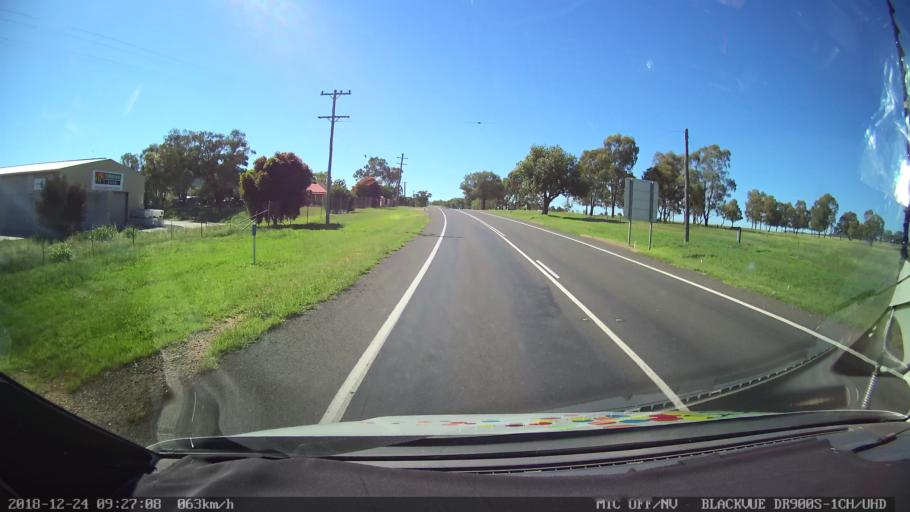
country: AU
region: New South Wales
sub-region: Liverpool Plains
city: Quirindi
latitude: -31.5254
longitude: 150.6793
